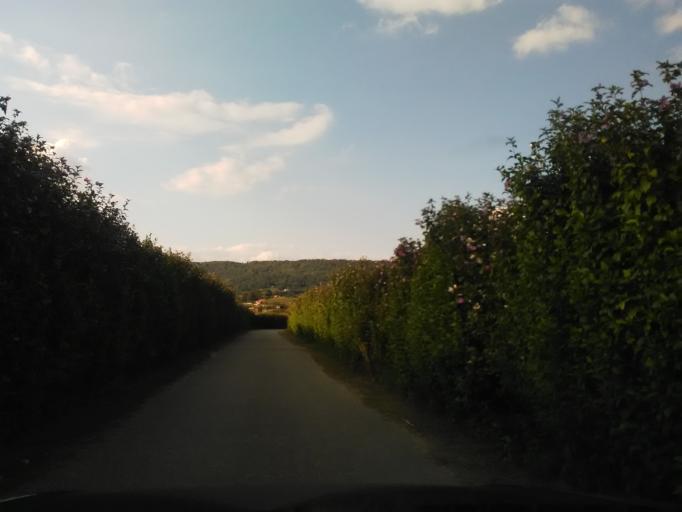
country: IT
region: Piedmont
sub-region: Provincia di Biella
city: Zimone
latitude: 45.4282
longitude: 8.0247
